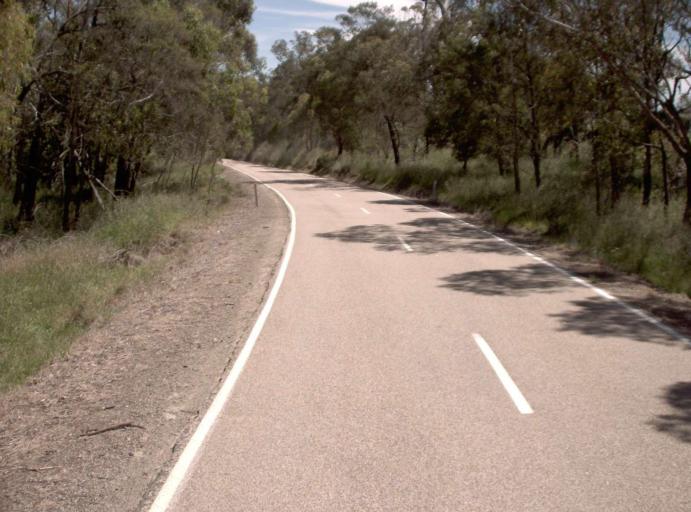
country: AU
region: Victoria
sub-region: East Gippsland
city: Lakes Entrance
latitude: -37.2734
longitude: 148.2560
